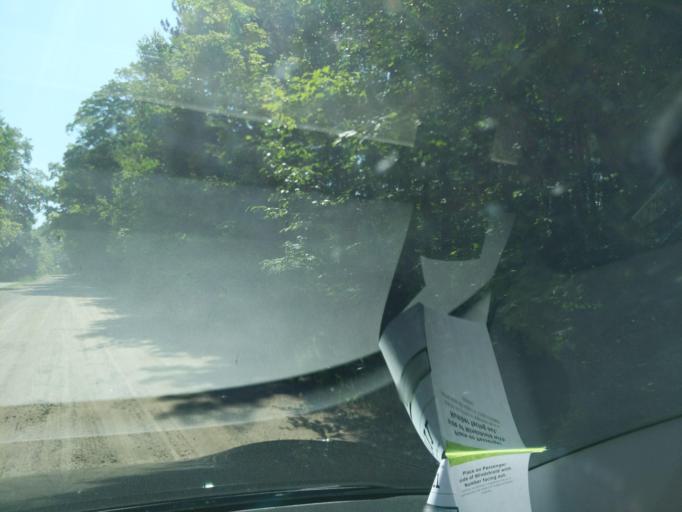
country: US
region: Michigan
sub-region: Mackinac County
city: Saint Ignace
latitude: 45.6793
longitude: -84.6727
